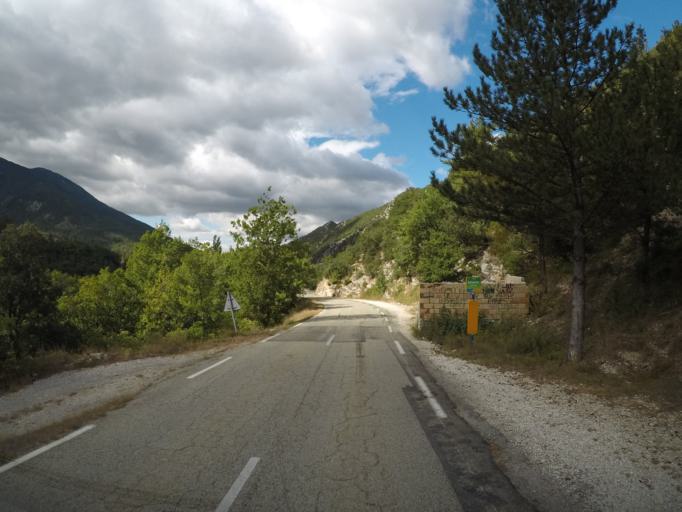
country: FR
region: Rhone-Alpes
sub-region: Departement de la Drome
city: Buis-les-Baronnies
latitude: 44.1898
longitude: 5.3360
